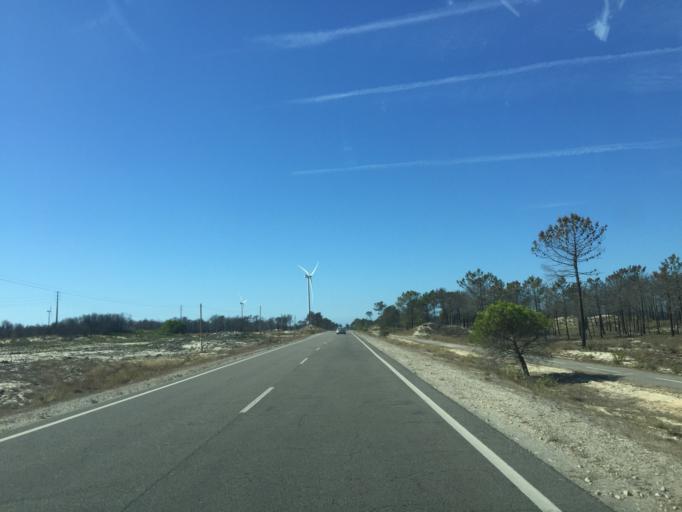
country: PT
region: Coimbra
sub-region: Mira
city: Mira
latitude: 40.3236
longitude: -8.7979
